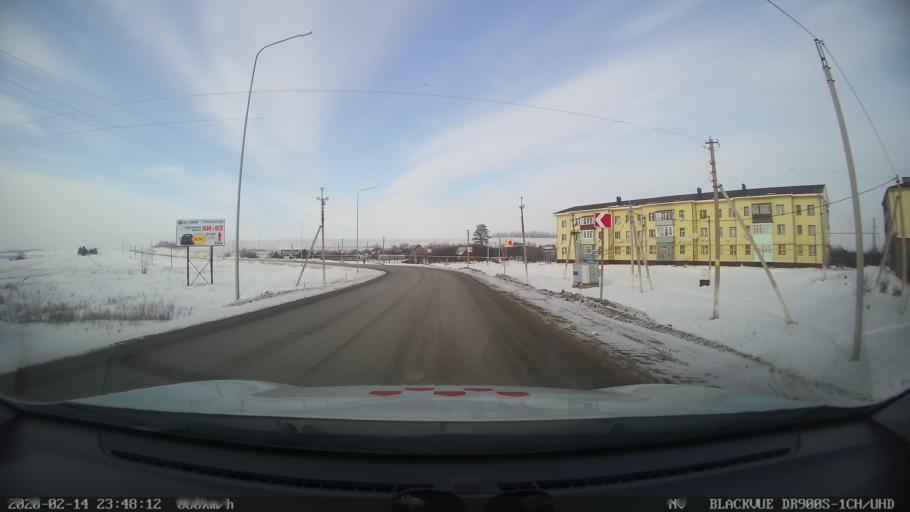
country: RU
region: Tatarstan
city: Kuybyshevskiy Zaton
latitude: 55.2464
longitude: 49.2059
